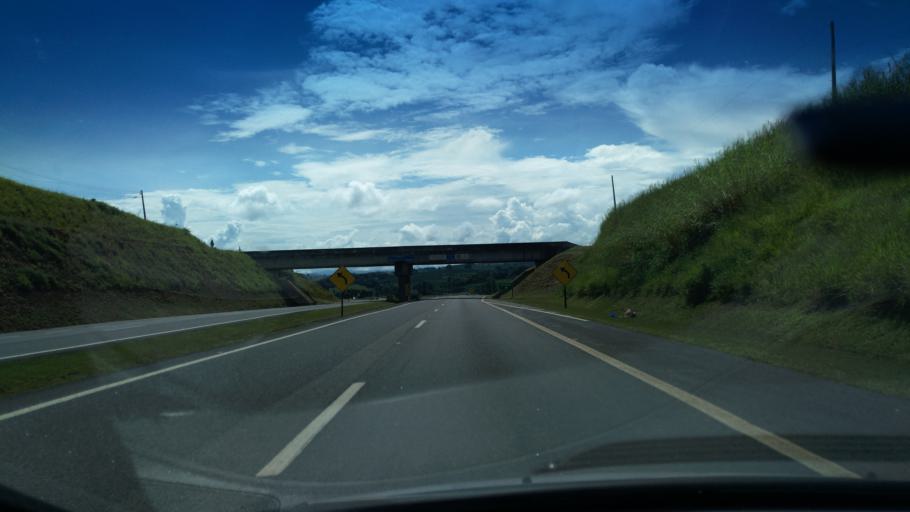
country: BR
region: Sao Paulo
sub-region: Santo Antonio Do Jardim
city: Espirito Santo do Pinhal
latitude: -22.2409
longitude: -46.8019
